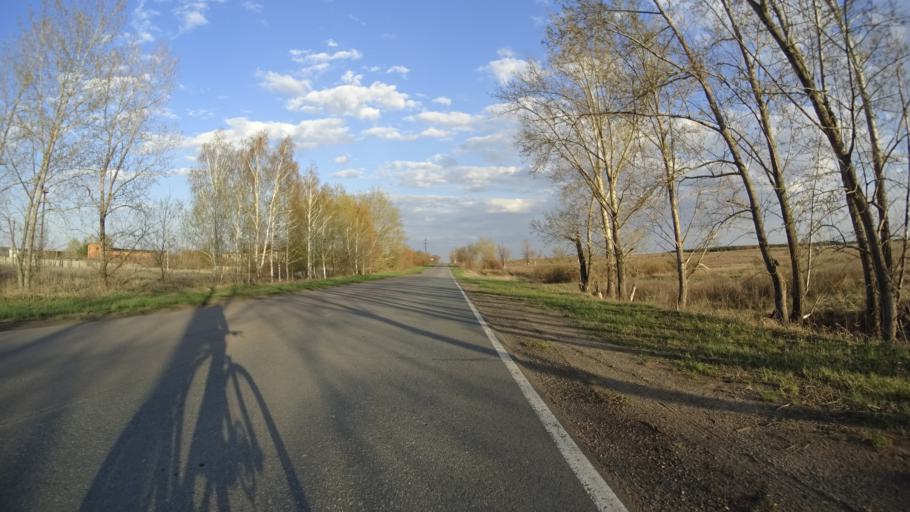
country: RU
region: Chelyabinsk
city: Troitsk
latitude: 54.0556
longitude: 61.5867
